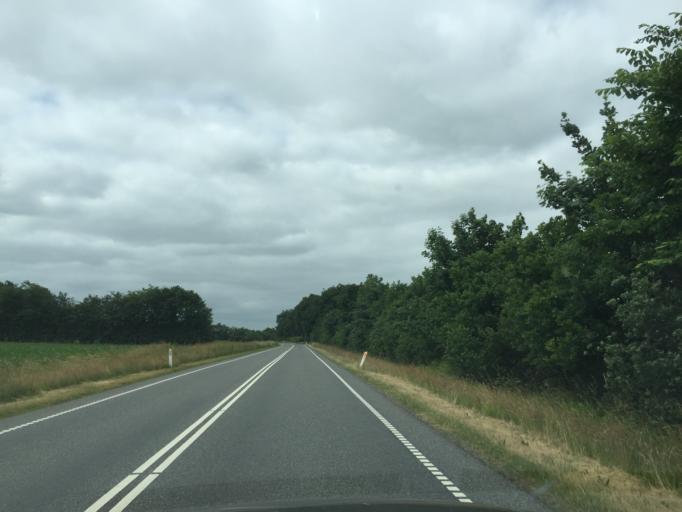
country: DK
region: South Denmark
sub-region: Vejen Kommune
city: Brorup
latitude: 55.4167
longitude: 8.9490
